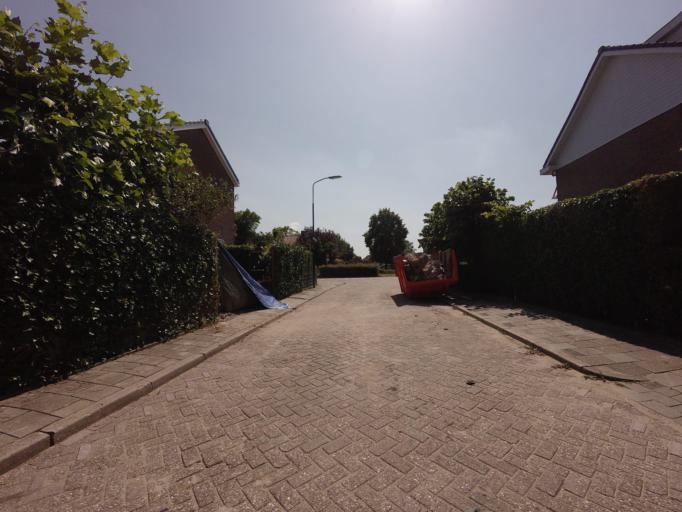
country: NL
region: Utrecht
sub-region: Gemeente Bunnik
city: Bunnik
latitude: 52.0650
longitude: 5.2057
